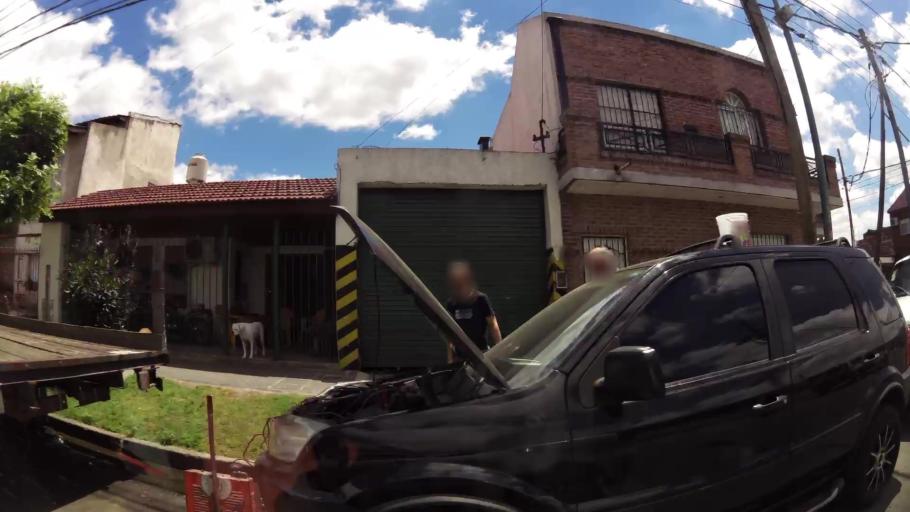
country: AR
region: Buenos Aires
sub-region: Partido de Lanus
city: Lanus
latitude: -34.7025
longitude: -58.4283
